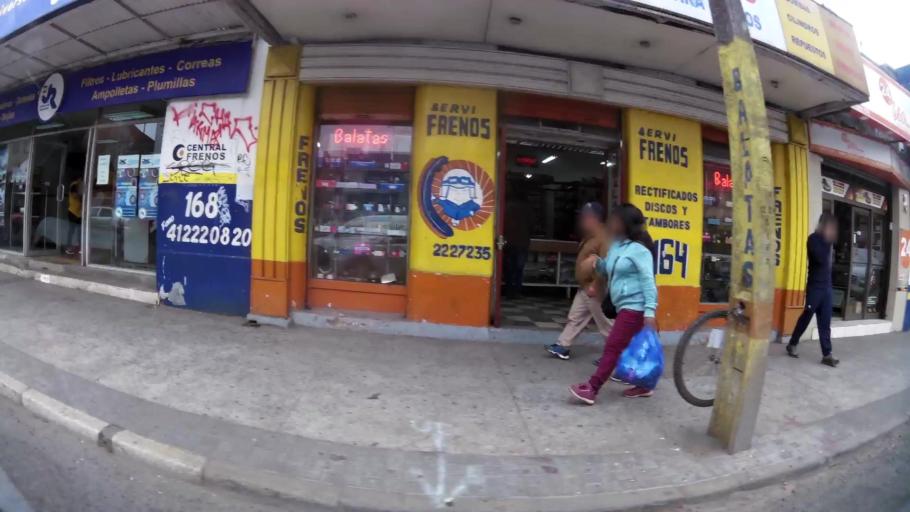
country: CL
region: Biobio
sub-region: Provincia de Concepcion
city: Concepcion
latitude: -36.8271
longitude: -73.0579
